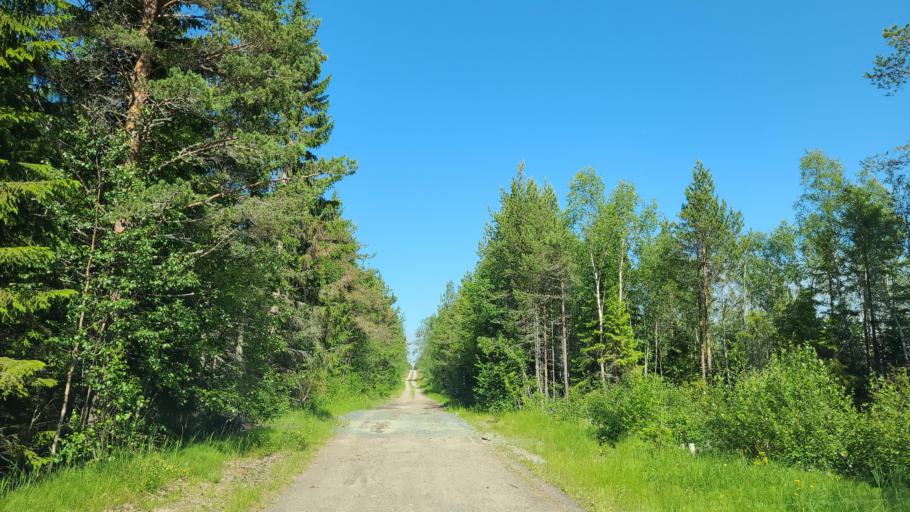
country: SE
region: Vaesternorrland
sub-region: OErnskoeldsviks Kommun
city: Husum
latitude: 63.4294
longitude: 19.2278
